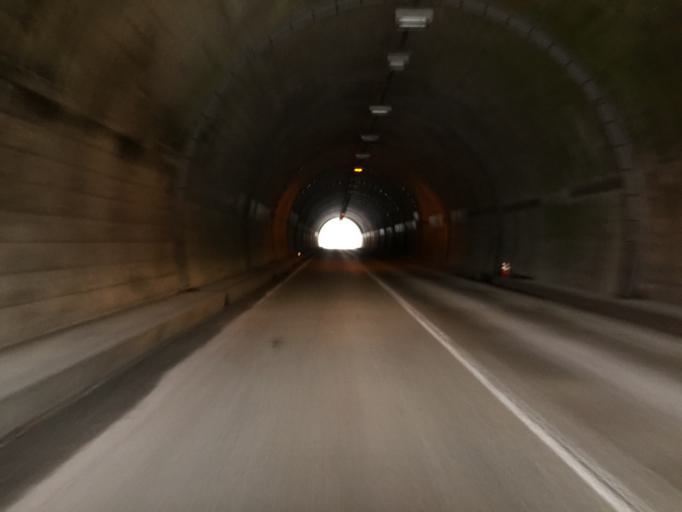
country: JP
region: Niigata
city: Tochio-honcho
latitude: 37.5185
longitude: 139.0964
